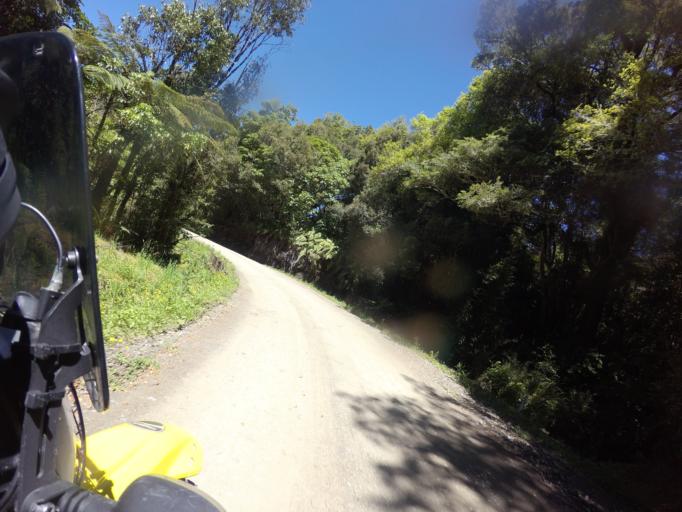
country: NZ
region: Bay of Plenty
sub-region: Opotiki District
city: Opotiki
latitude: -38.4105
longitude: 177.4127
